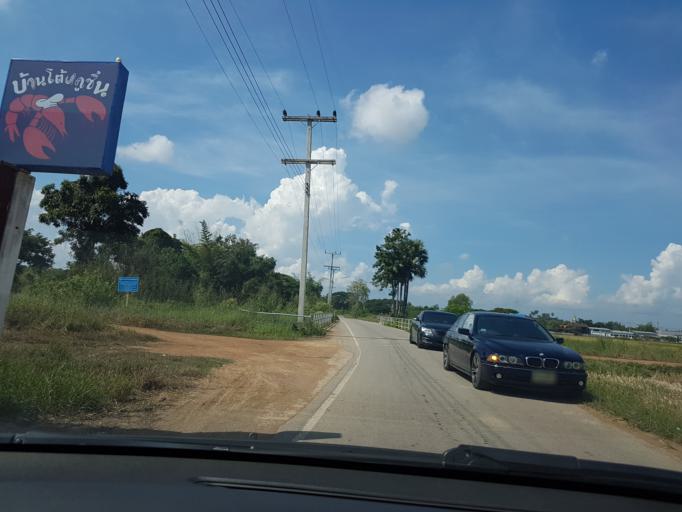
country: TH
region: Lampang
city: Ko Kha
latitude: 18.2105
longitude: 99.3955
